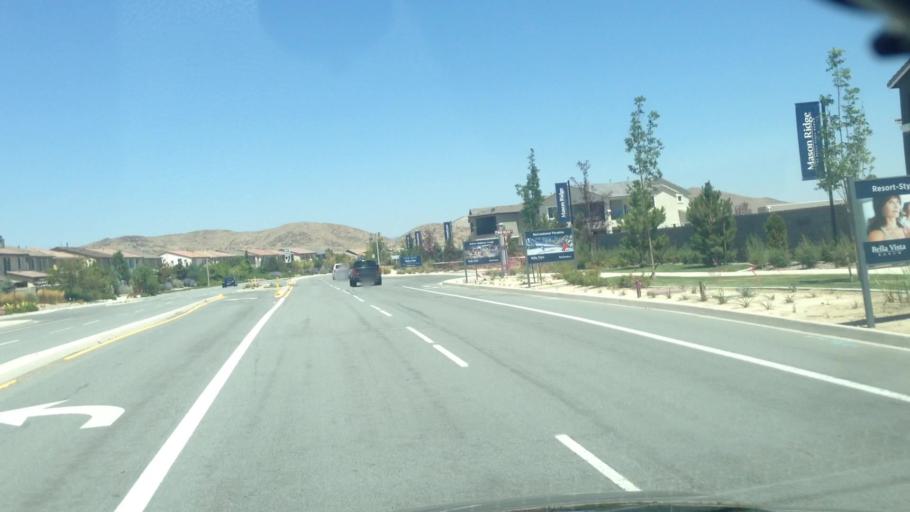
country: US
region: Nevada
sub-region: Washoe County
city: Sparks
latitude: 39.4462
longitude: -119.7273
